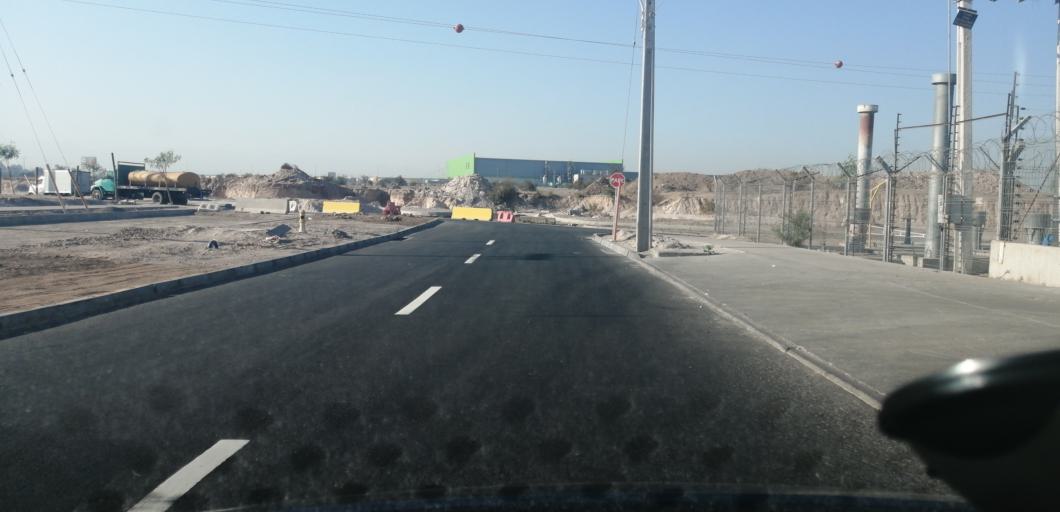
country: CL
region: Santiago Metropolitan
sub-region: Provincia de Santiago
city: Lo Prado
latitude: -33.4372
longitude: -70.7877
